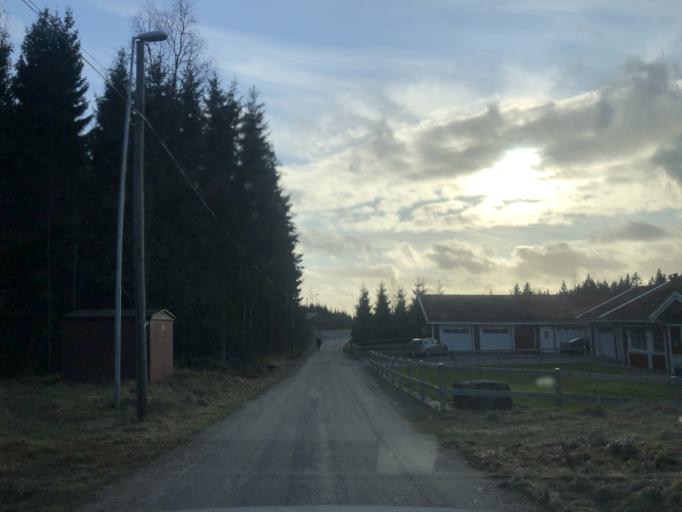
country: SE
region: Vaestra Goetaland
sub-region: Ulricehamns Kommun
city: Ulricehamn
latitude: 57.7756
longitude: 13.4346
